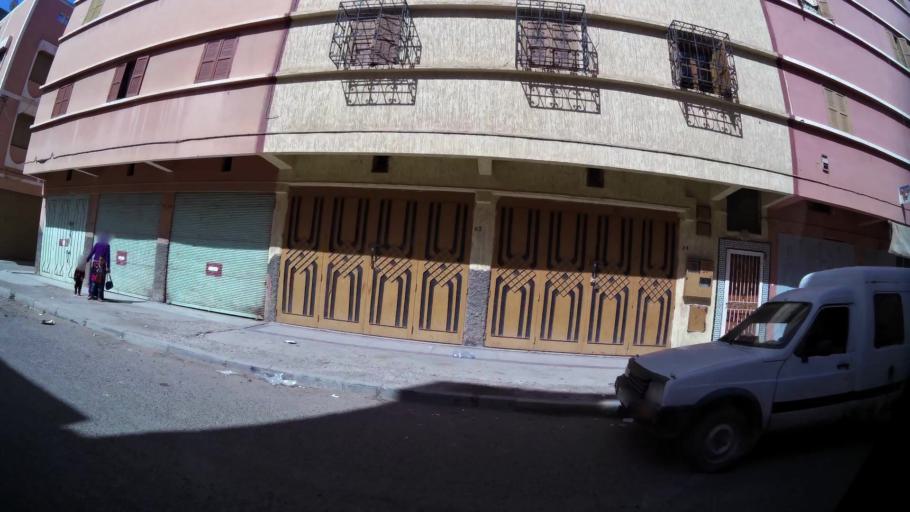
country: MA
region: Souss-Massa-Draa
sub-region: Inezgane-Ait Mellou
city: Inezgane
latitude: 30.3452
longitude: -9.5062
